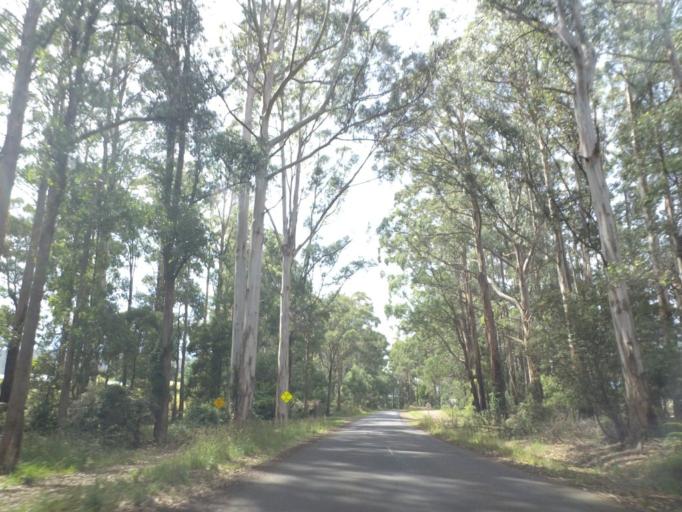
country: AU
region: Victoria
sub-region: Yarra Ranges
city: Healesville
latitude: -37.5509
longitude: 145.4949
